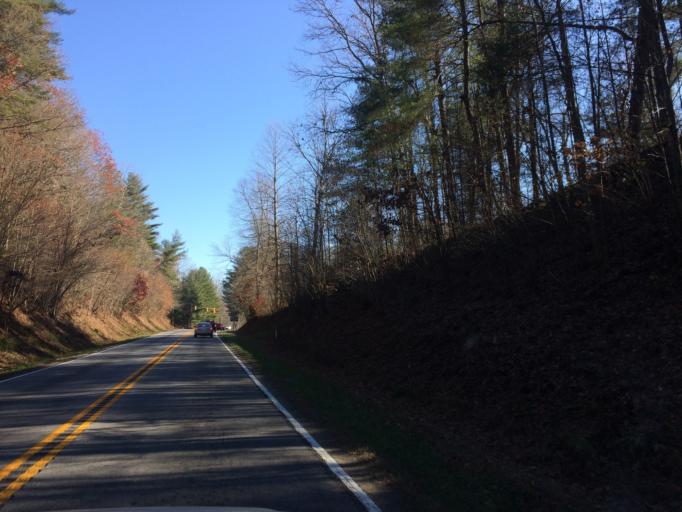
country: US
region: North Carolina
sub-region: Henderson County
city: Mountain Home
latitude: 35.3686
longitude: -82.5257
